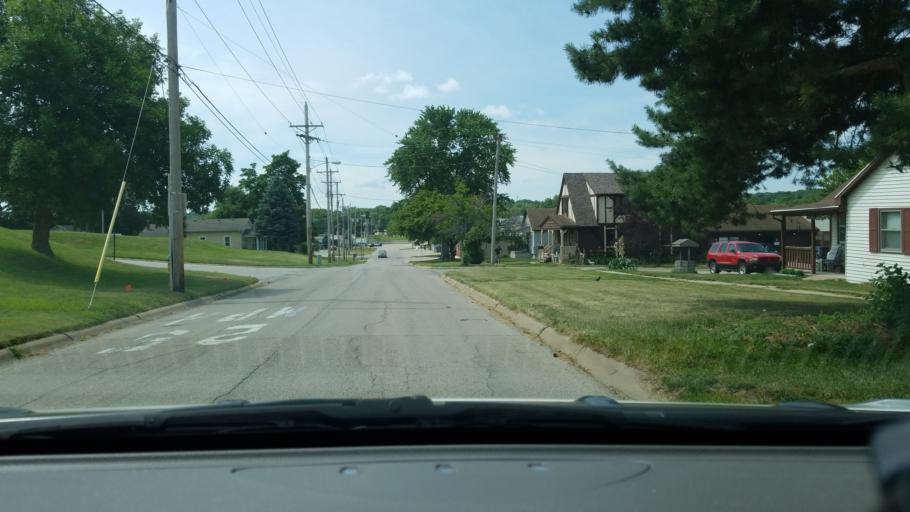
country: US
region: Nebraska
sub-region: Sarpy County
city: Papillion
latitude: 41.1598
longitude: -96.0443
